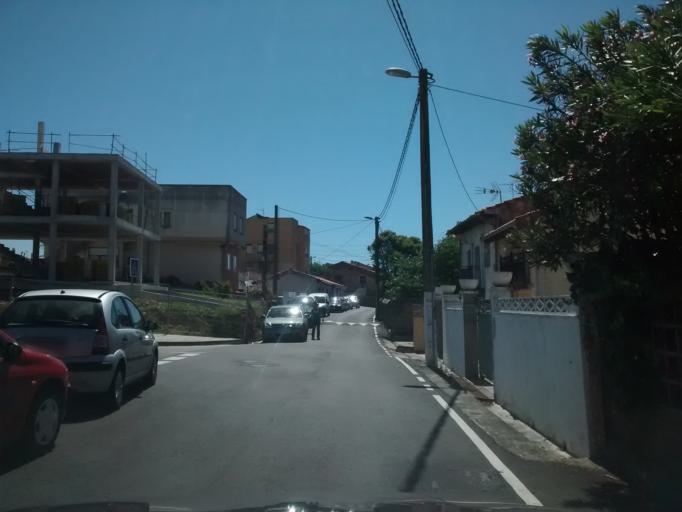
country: ES
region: Cantabria
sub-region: Provincia de Cantabria
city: Santander
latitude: 43.4819
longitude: -3.8022
